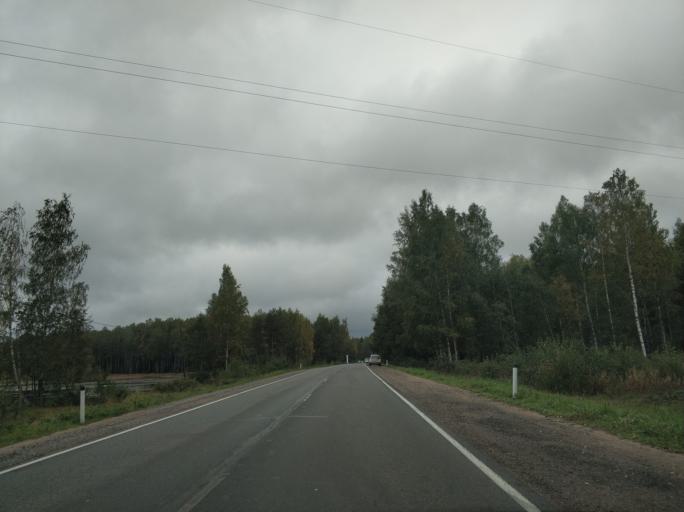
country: RU
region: Leningrad
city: Borisova Griva
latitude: 60.0882
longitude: 30.8689
